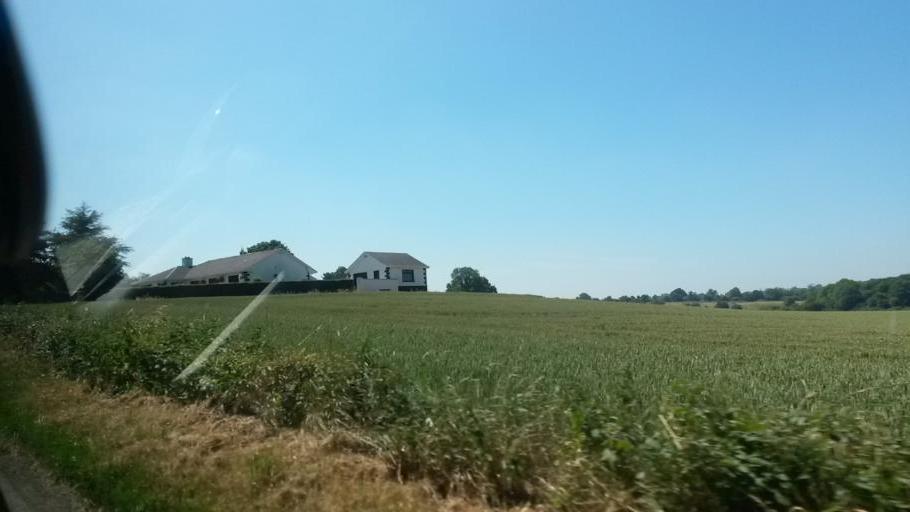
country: IE
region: Leinster
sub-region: An Mhi
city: Stamullin
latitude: 53.5834
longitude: -6.3024
